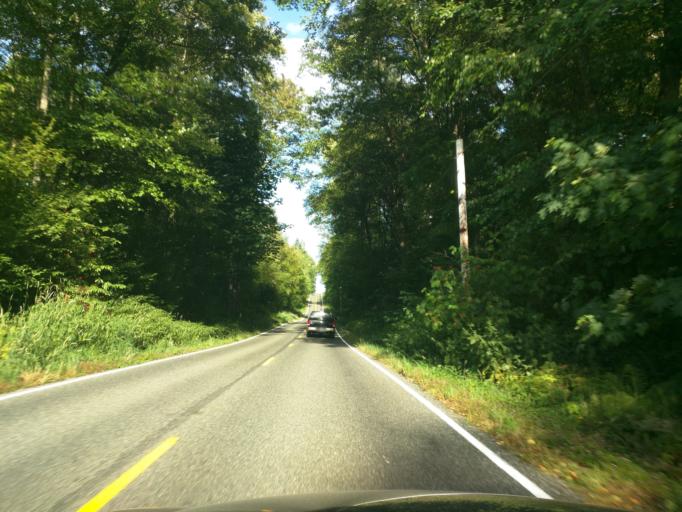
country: CA
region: British Columbia
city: Langley
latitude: 48.9935
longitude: -122.6310
